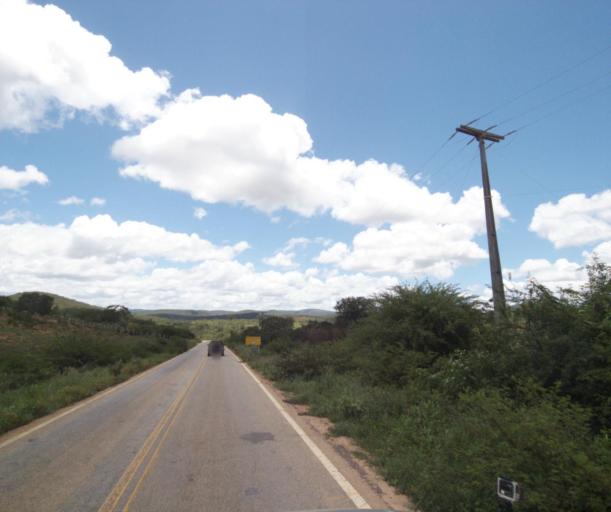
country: BR
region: Bahia
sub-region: Pocoes
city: Pocoes
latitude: -14.3804
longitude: -40.5106
